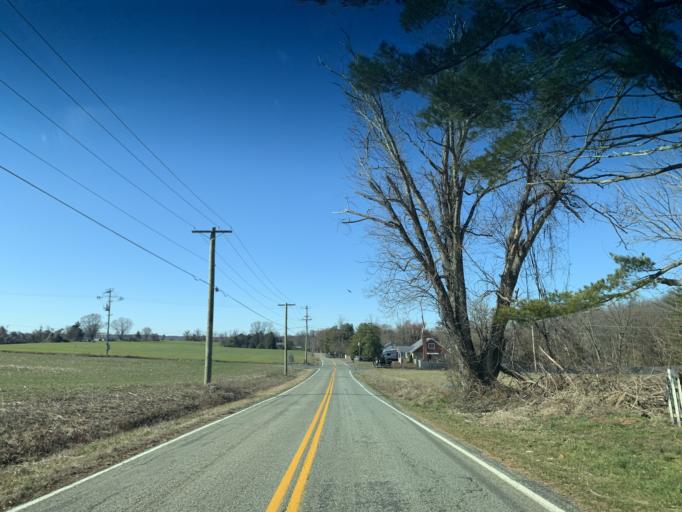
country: US
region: Maryland
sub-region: Cecil County
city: Rising Sun
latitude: 39.6809
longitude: -76.0996
